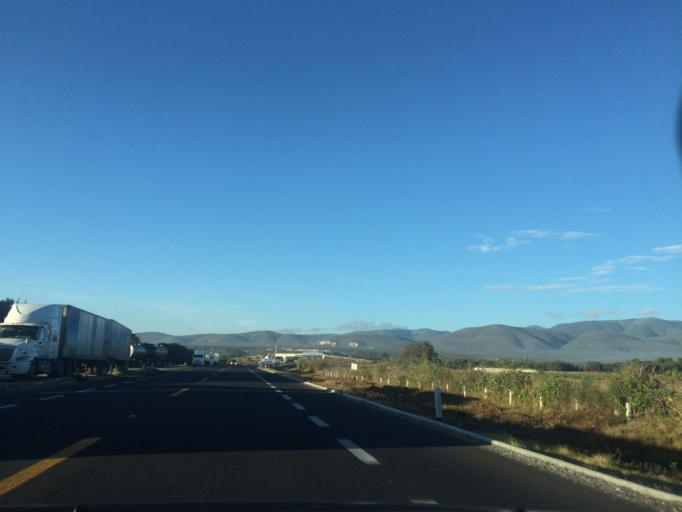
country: MX
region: Puebla
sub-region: Santiago Miahuatlan
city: San Jose Monte Chiquito
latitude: 18.4977
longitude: -97.4544
